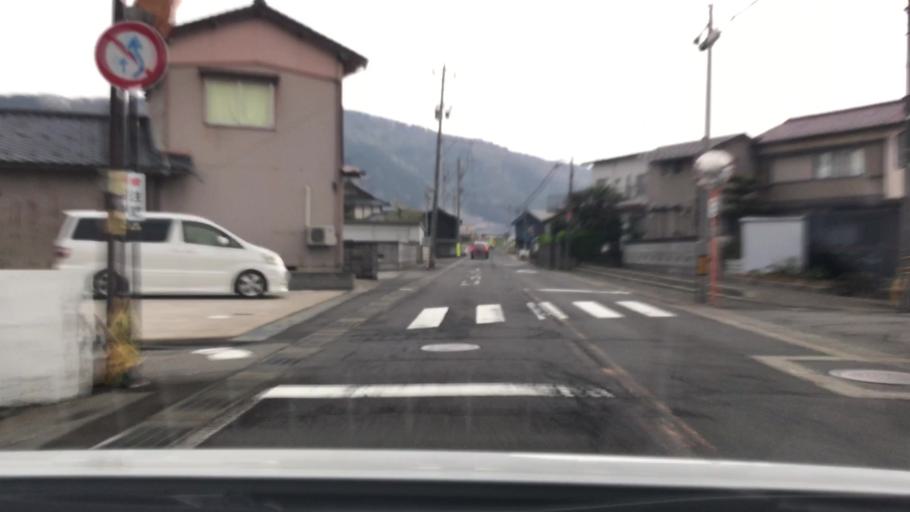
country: JP
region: Fukui
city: Fukui-shi
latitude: 36.0861
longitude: 136.1895
